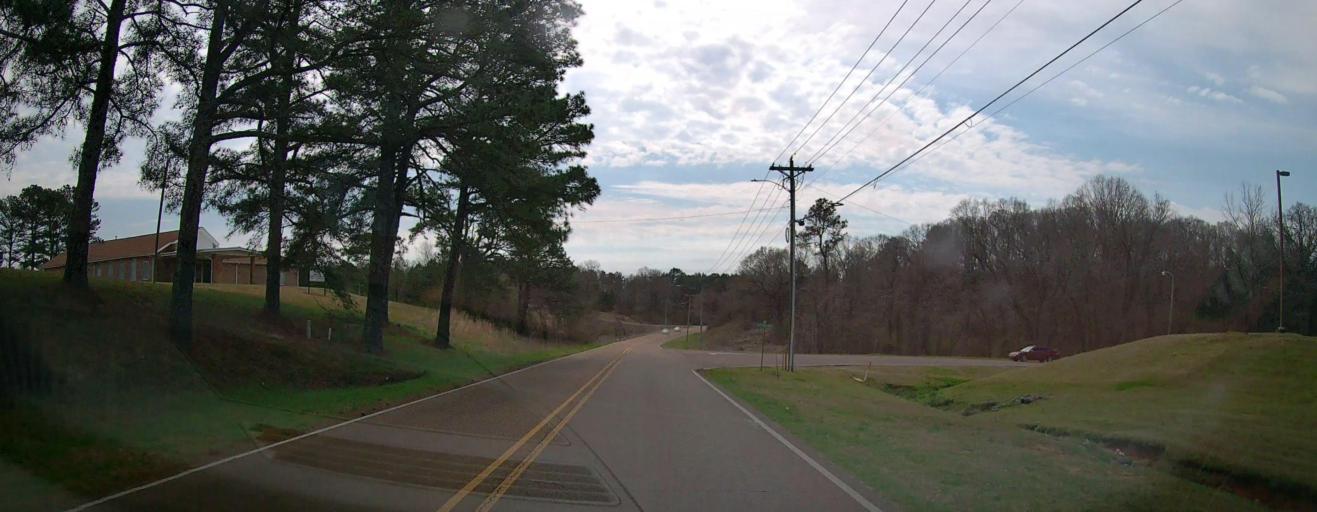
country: US
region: Mississippi
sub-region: Marshall County
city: Holly Springs
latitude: 34.7599
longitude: -89.4298
